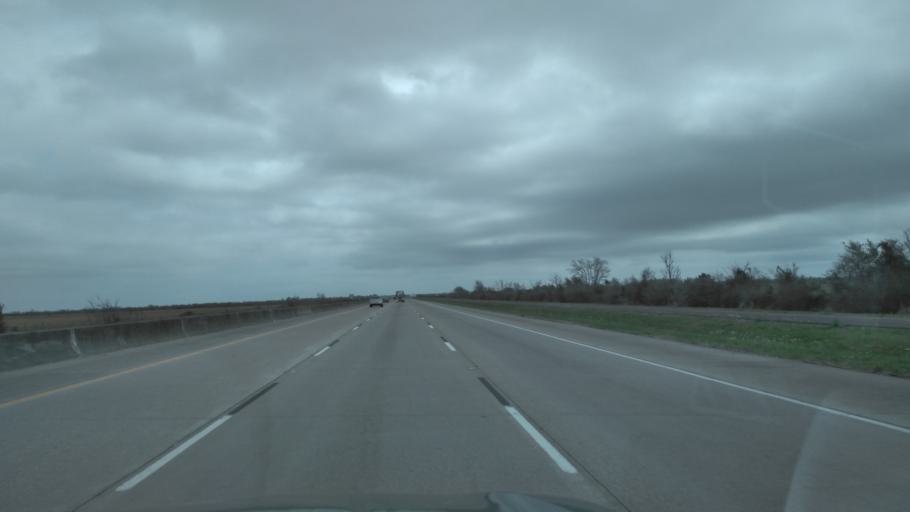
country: US
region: Texas
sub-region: Chambers County
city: Winnie
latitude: 29.8287
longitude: -94.4637
